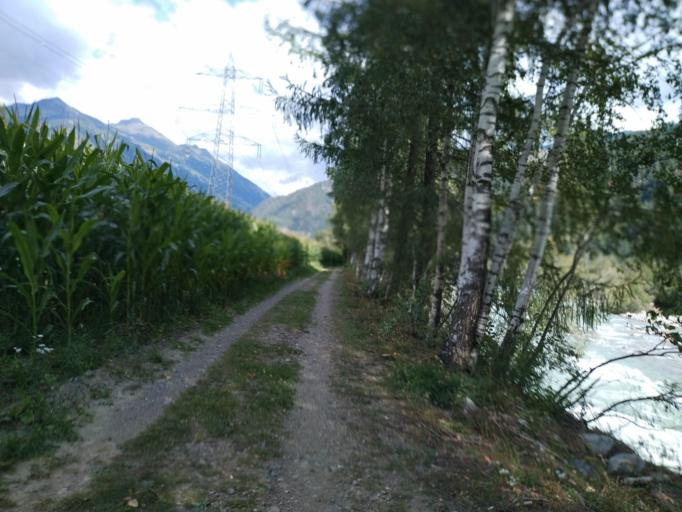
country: AT
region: Tyrol
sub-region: Politischer Bezirk Lienz
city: Schlaiten
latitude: 46.9159
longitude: 12.6068
